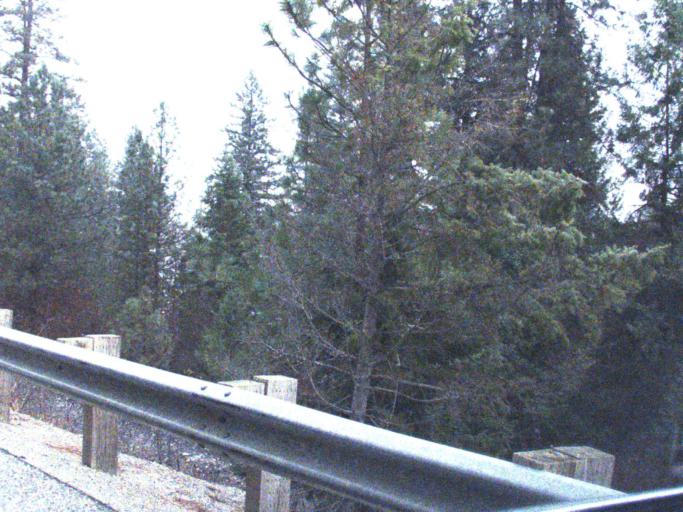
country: CA
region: British Columbia
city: Grand Forks
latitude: 48.8781
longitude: -118.2152
